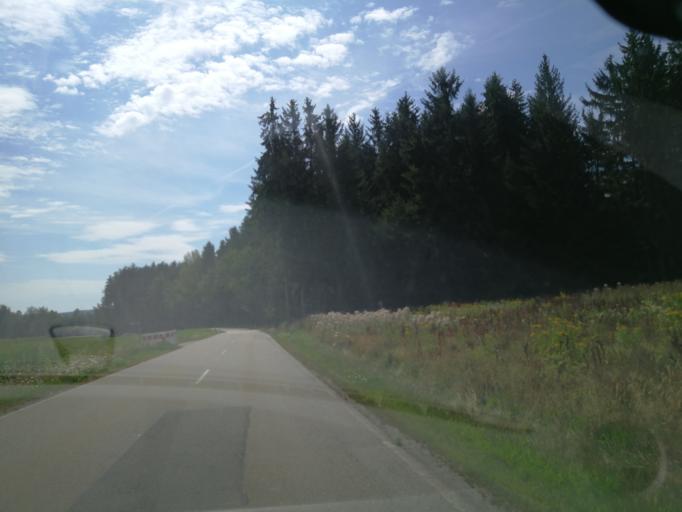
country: DE
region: Bavaria
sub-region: Lower Bavaria
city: Wiesenfelden
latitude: 49.0512
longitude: 12.5219
